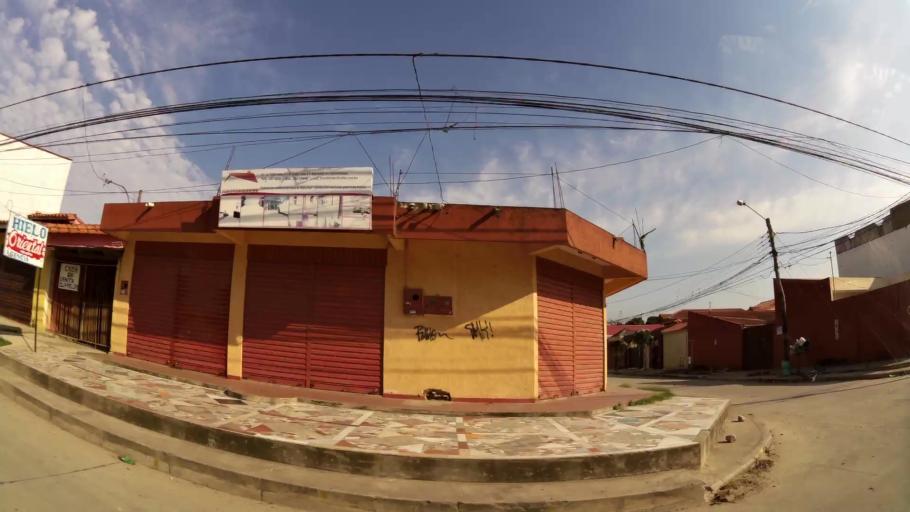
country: BO
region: Santa Cruz
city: Santa Cruz de la Sierra
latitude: -17.7524
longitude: -63.1534
